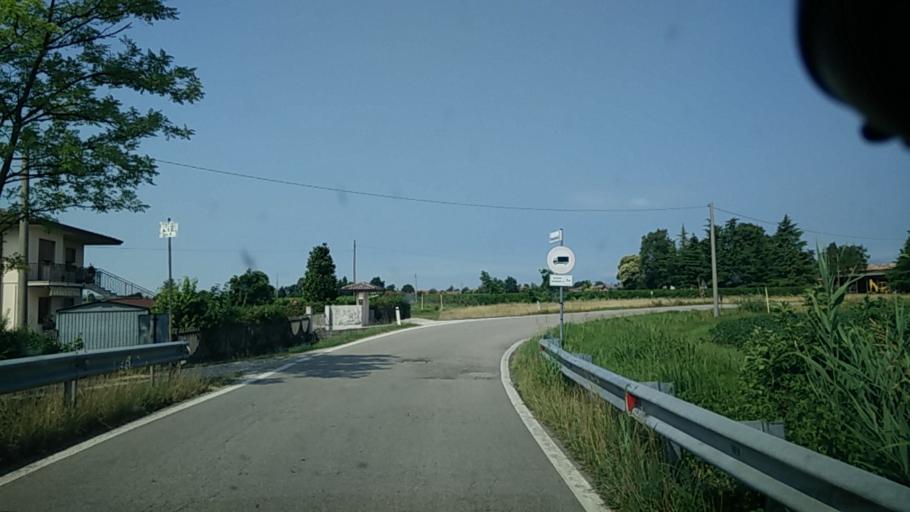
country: IT
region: Veneto
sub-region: Provincia di Treviso
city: Fontanelle
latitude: 45.8459
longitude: 12.4886
